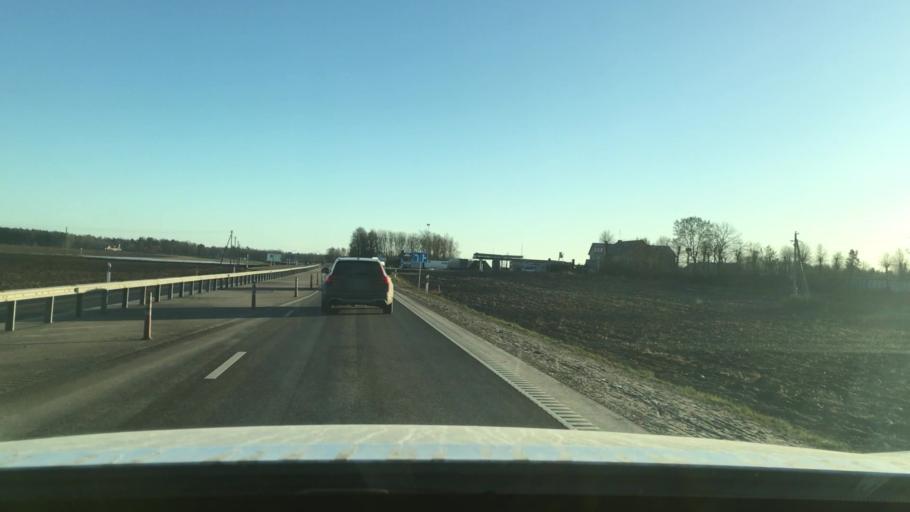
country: LT
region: Panevezys
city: Pasvalys
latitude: 56.2698
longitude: 24.3700
